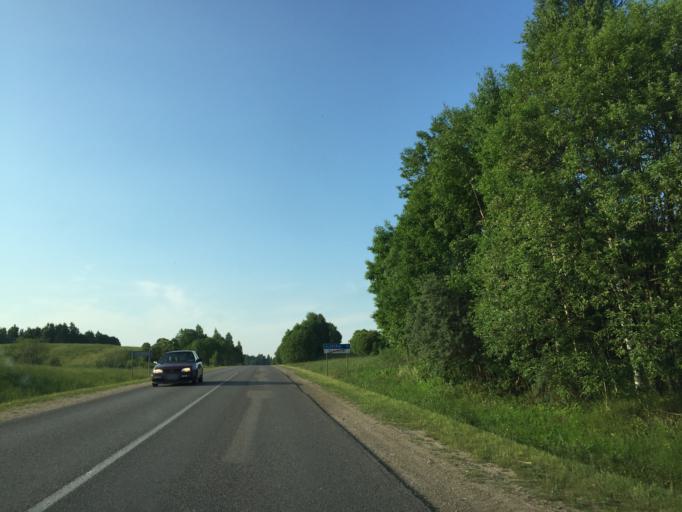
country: LT
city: Plateliai
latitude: 56.0531
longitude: 21.8193
